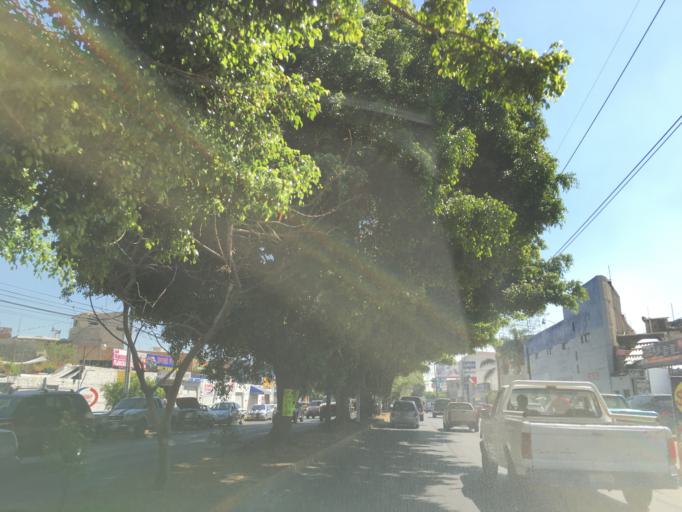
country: MX
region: Jalisco
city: Guadalajara
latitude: 20.6329
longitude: -103.4017
